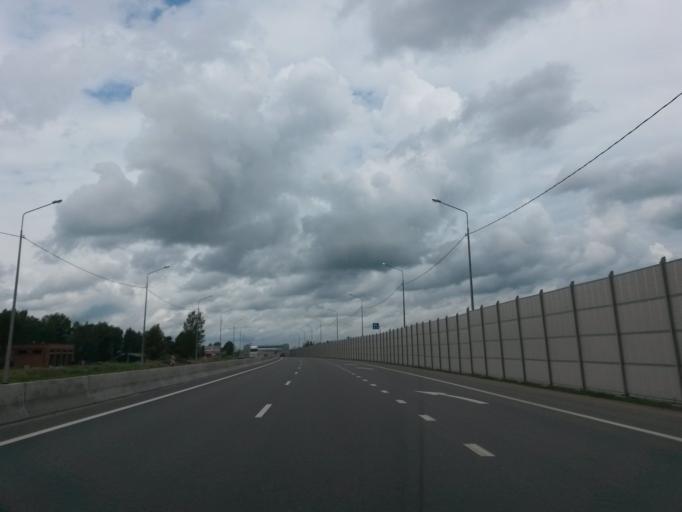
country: RU
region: Jaroslavl
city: Yaroslavl
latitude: 57.7117
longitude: 39.9034
